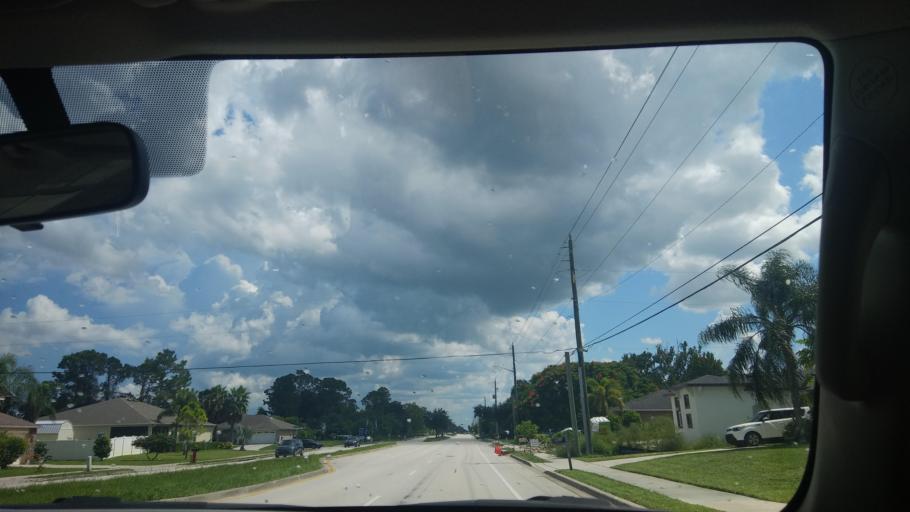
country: US
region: Florida
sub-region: Brevard County
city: Palm Bay
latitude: 27.9919
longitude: -80.6486
